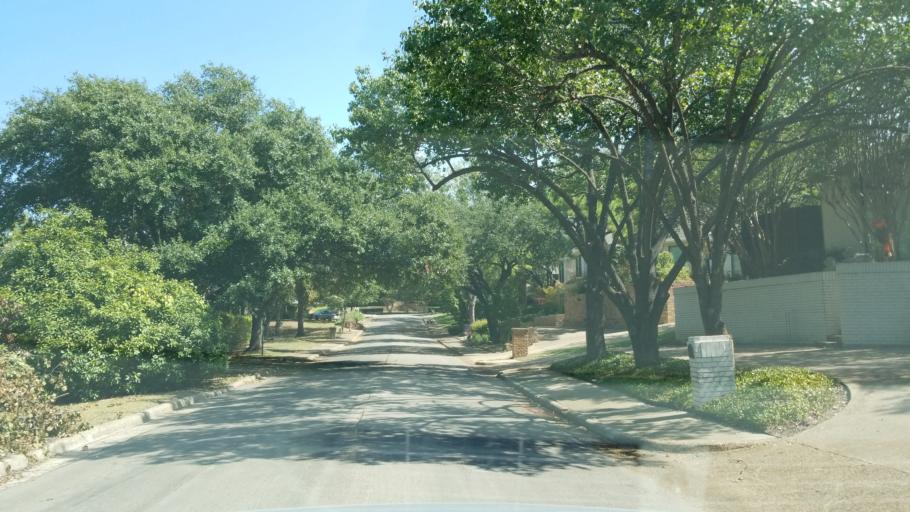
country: US
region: Texas
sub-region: Dallas County
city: Addison
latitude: 32.9646
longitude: -96.8032
